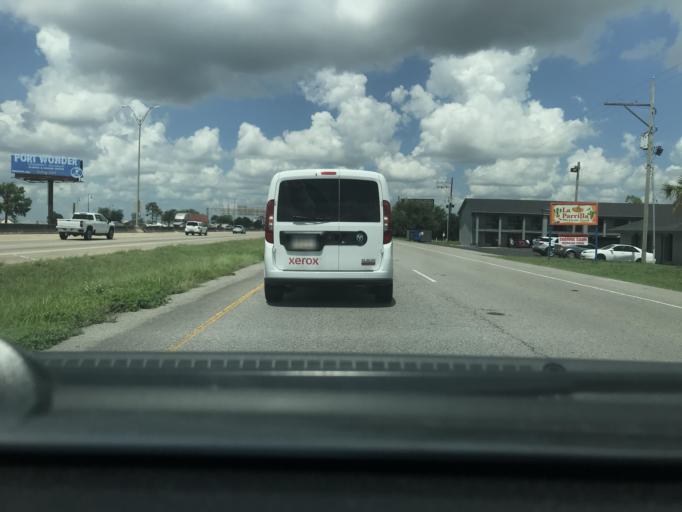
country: US
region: Louisiana
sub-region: Calcasieu Parish
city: Westlake
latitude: 30.2374
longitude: -93.2298
